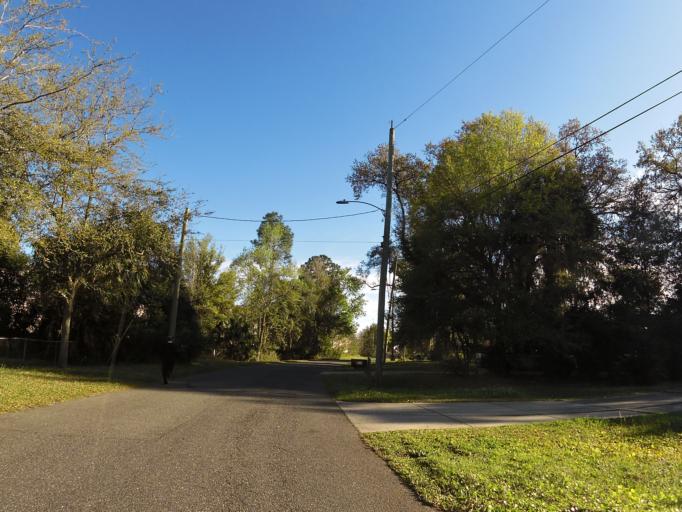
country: US
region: Florida
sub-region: Duval County
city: Jacksonville
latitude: 30.3980
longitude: -81.6686
